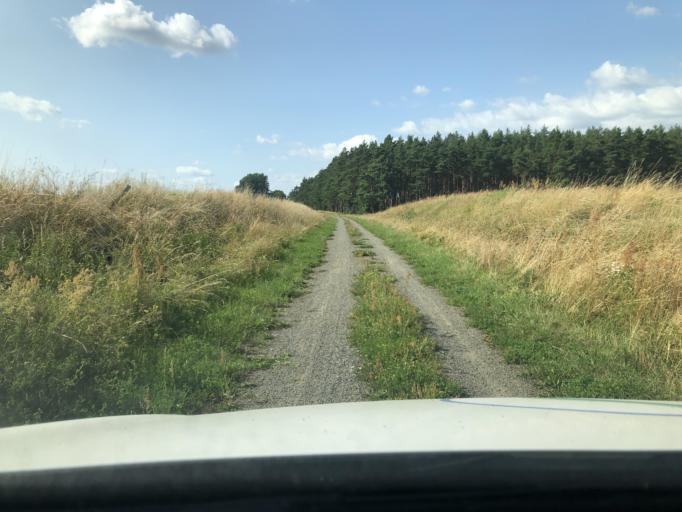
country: SE
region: Skane
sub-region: Kristianstads Kommun
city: Degeberga
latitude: 55.8133
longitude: 14.1300
